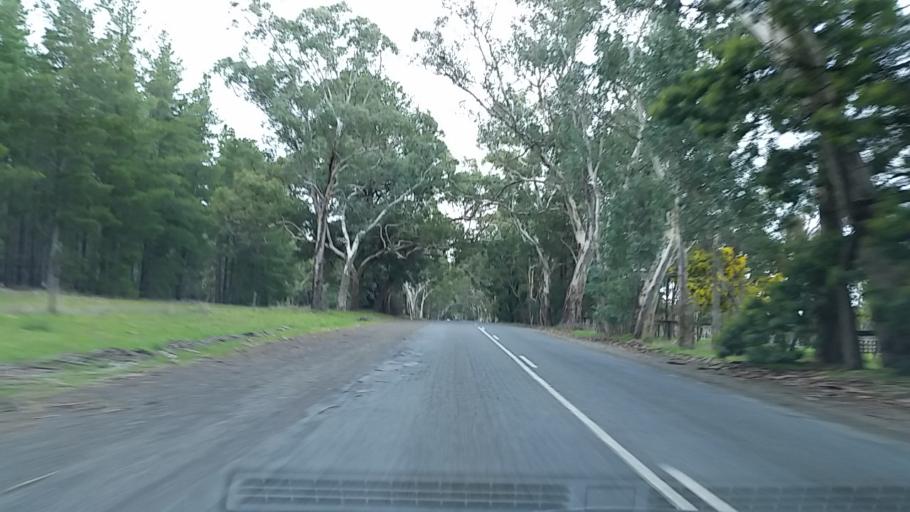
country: AU
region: South Australia
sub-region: Mount Barker
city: Meadows
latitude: -35.2373
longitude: 138.6765
